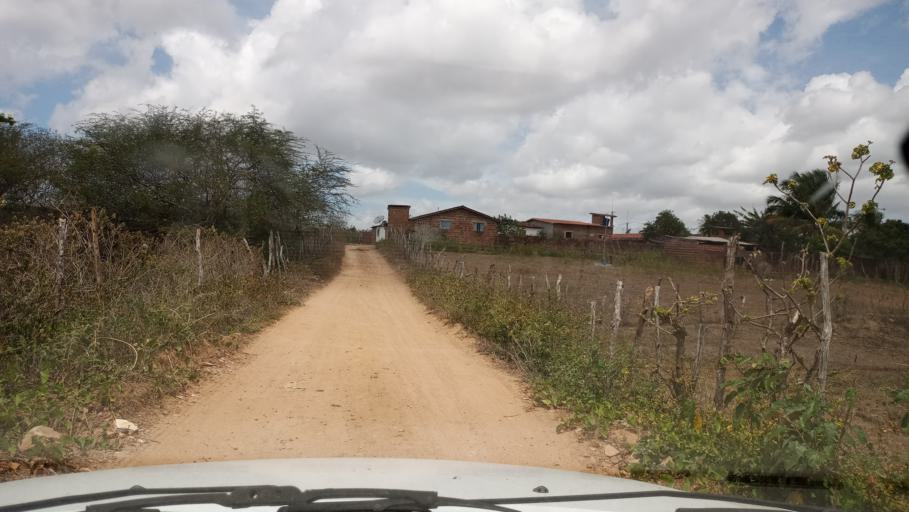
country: BR
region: Rio Grande do Norte
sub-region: Goianinha
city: Goianinha
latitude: -6.3025
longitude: -35.2748
